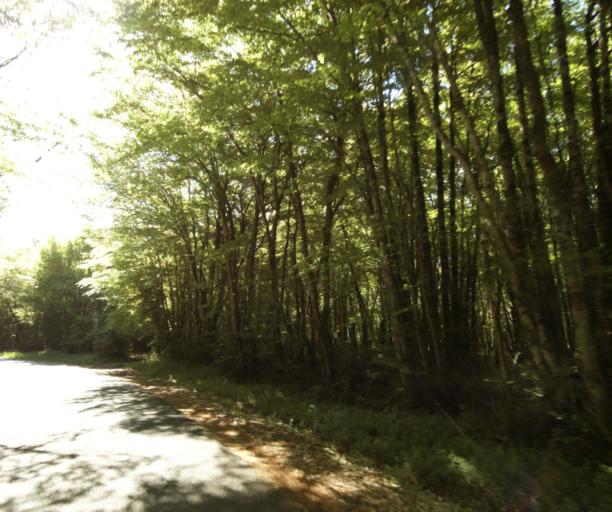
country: FR
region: Poitou-Charentes
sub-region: Departement de la Charente-Maritime
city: Bussac-sur-Charente
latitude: 45.8047
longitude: -0.6656
